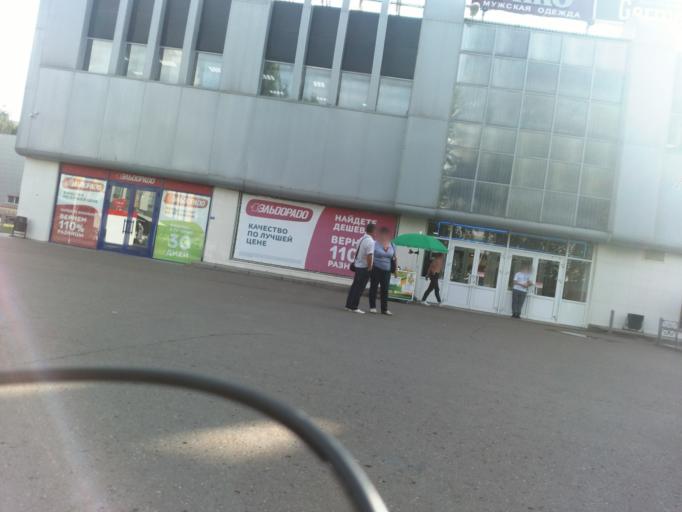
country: RU
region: Tatarstan
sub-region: Tukayevskiy Rayon
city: Naberezhnyye Chelny
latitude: 55.7448
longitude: 52.4219
